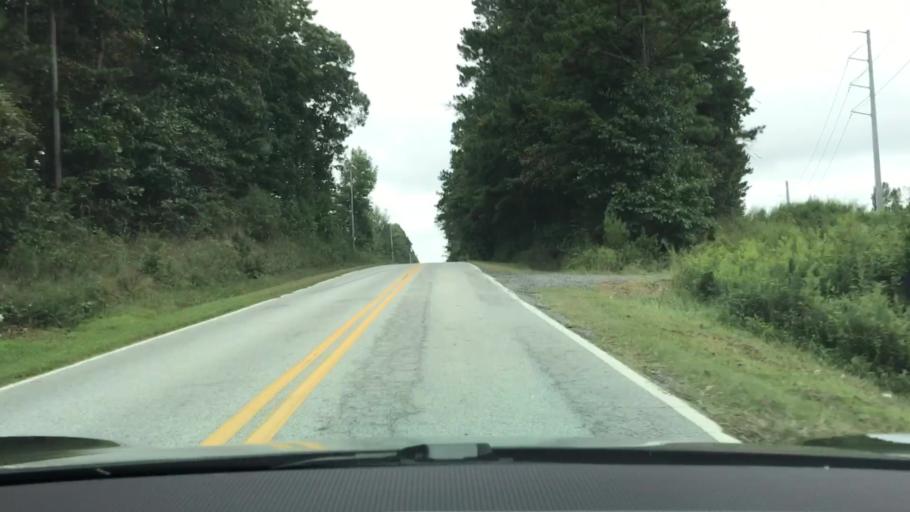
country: US
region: Georgia
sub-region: Barrow County
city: Auburn
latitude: 34.0519
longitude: -83.8192
